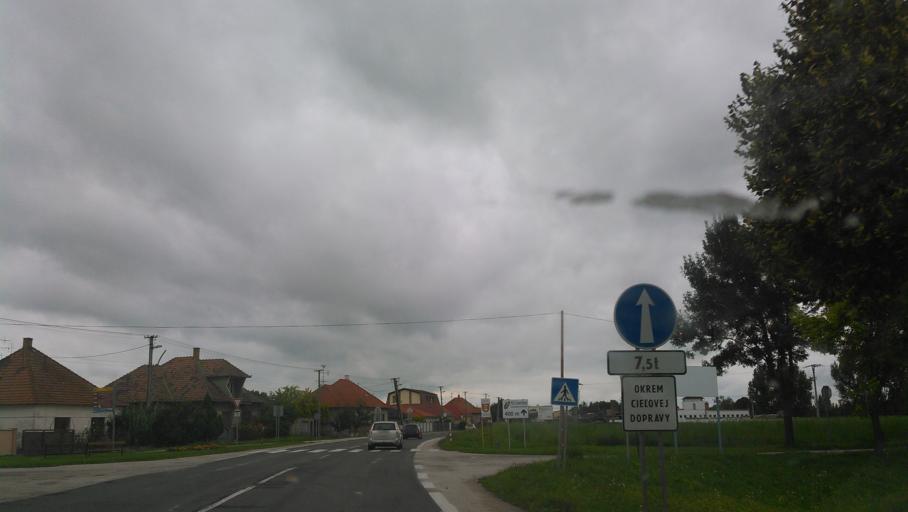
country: SK
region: Trnavsky
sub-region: Okres Dunajska Streda
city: Velky Meder
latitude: 47.9371
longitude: 17.7188
